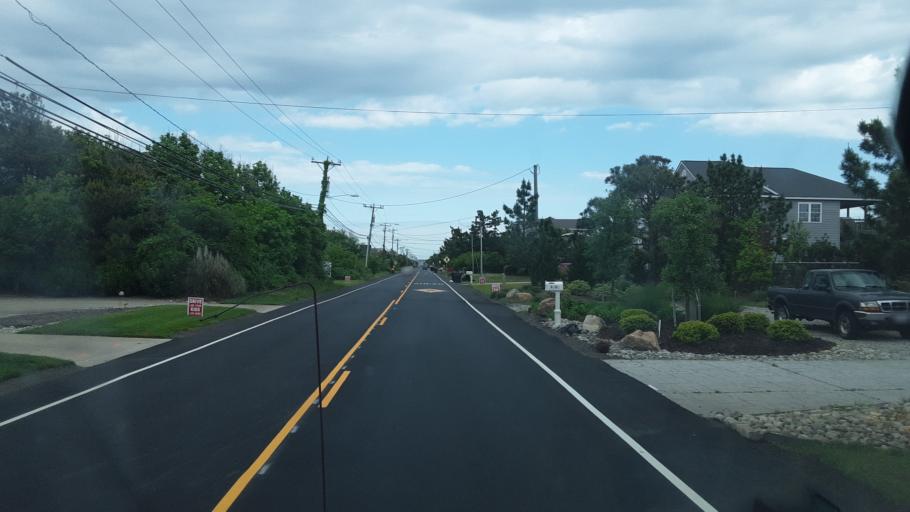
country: US
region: Virginia
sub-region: City of Virginia Beach
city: Virginia Beach
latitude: 36.7234
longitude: -75.9366
